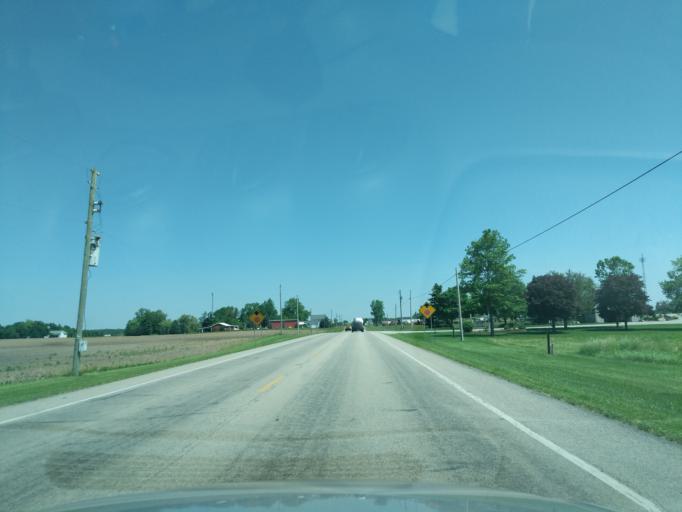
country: US
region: Indiana
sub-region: Whitley County
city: Columbia City
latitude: 41.0730
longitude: -85.4703
